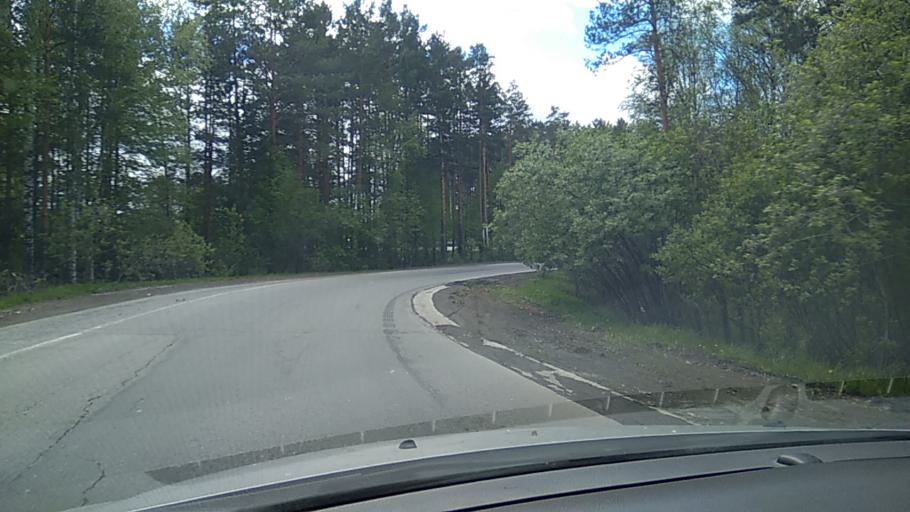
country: RU
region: Sverdlovsk
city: Istok
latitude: 56.8038
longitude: 60.7930
